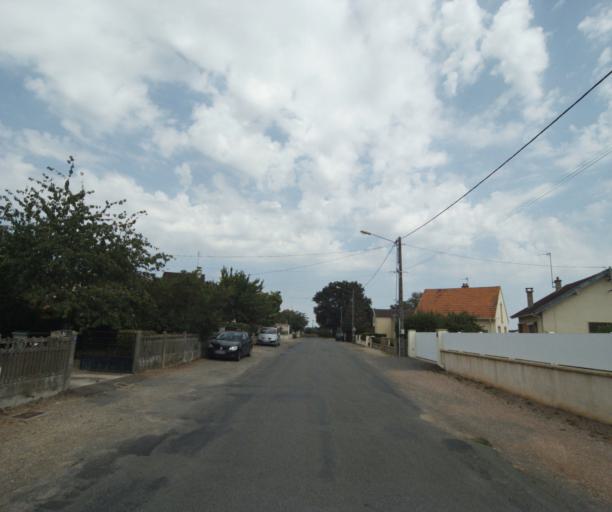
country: FR
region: Bourgogne
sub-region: Departement de Saone-et-Loire
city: Gueugnon
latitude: 46.5942
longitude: 4.0430
